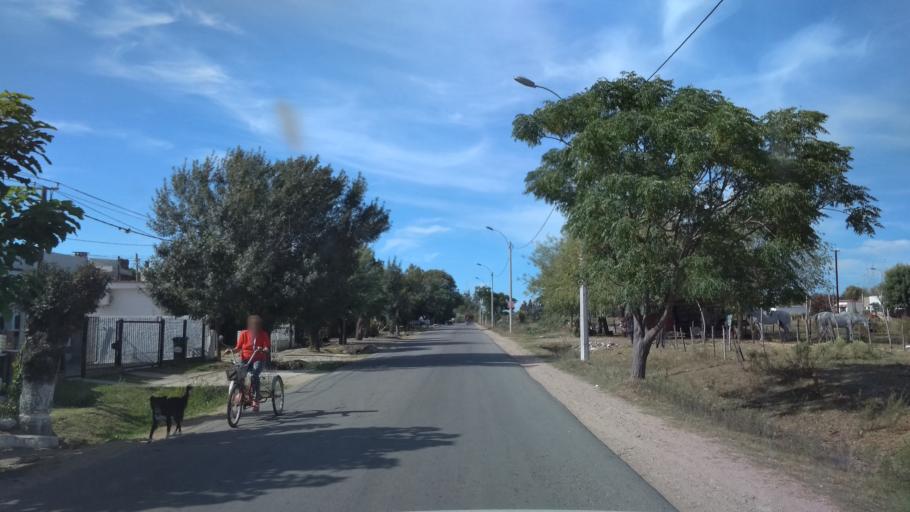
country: UY
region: Canelones
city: San Ramon
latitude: -34.2944
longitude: -55.9601
